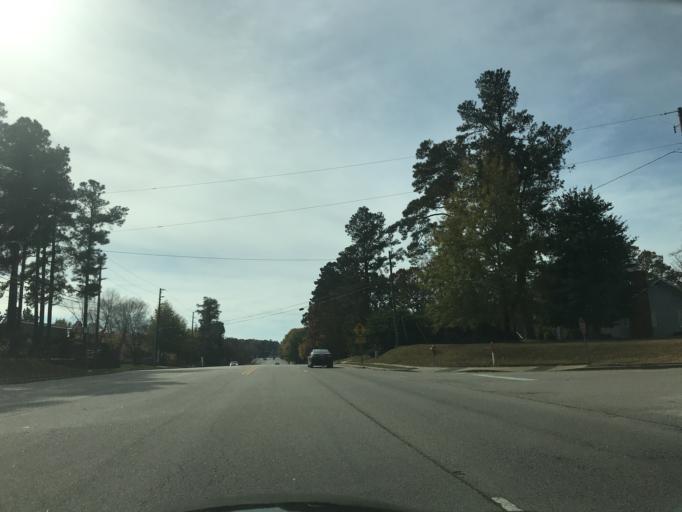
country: US
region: North Carolina
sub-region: Wake County
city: West Raleigh
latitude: 35.8281
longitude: -78.7031
